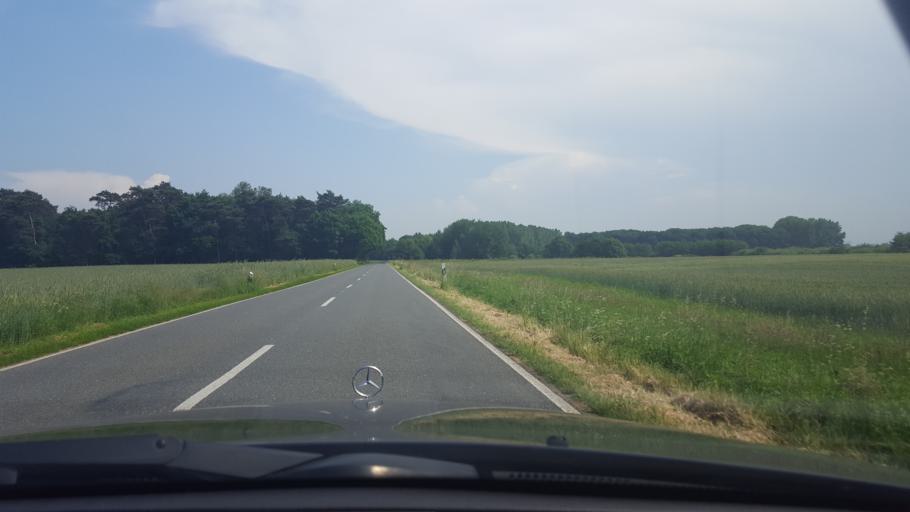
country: DE
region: North Rhine-Westphalia
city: Olfen
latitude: 51.7235
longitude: 7.2983
